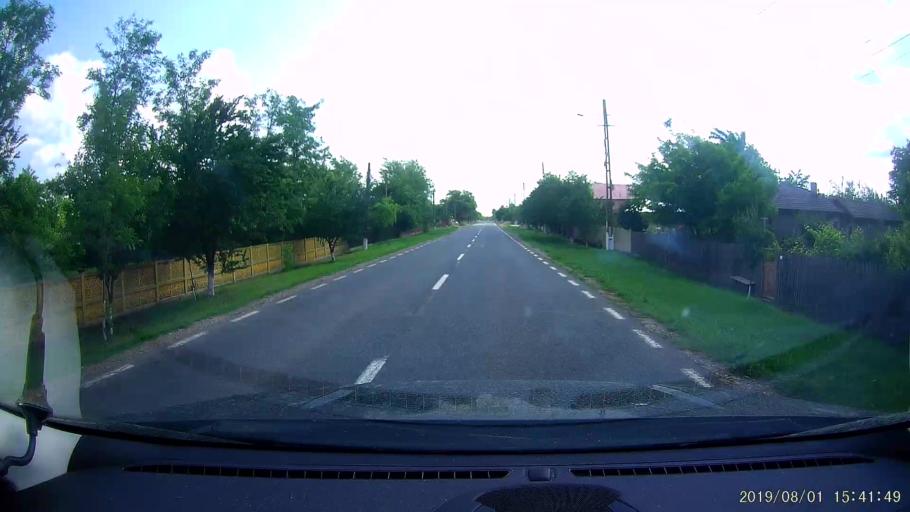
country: RO
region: Braila
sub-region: Comuna Baraganul
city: Baraganul
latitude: 44.8184
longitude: 27.5214
